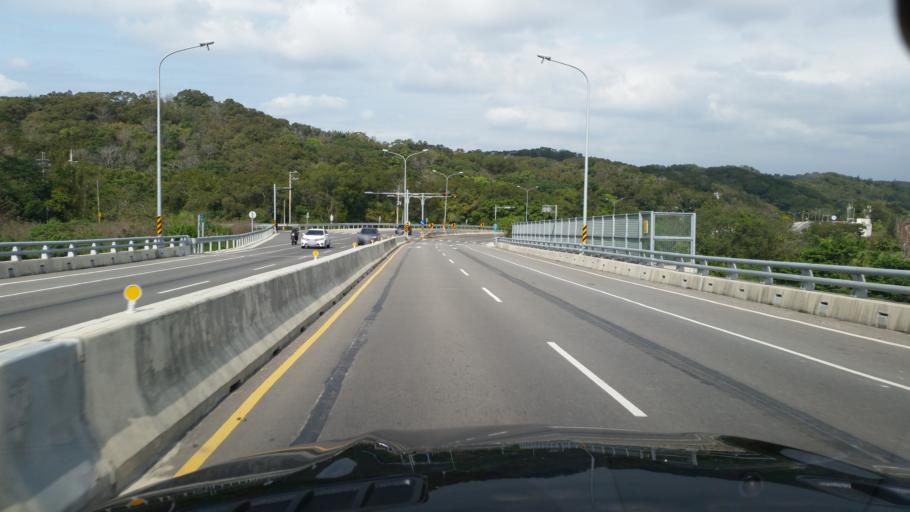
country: TW
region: Taiwan
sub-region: Miaoli
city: Miaoli
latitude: 24.6275
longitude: 120.8529
